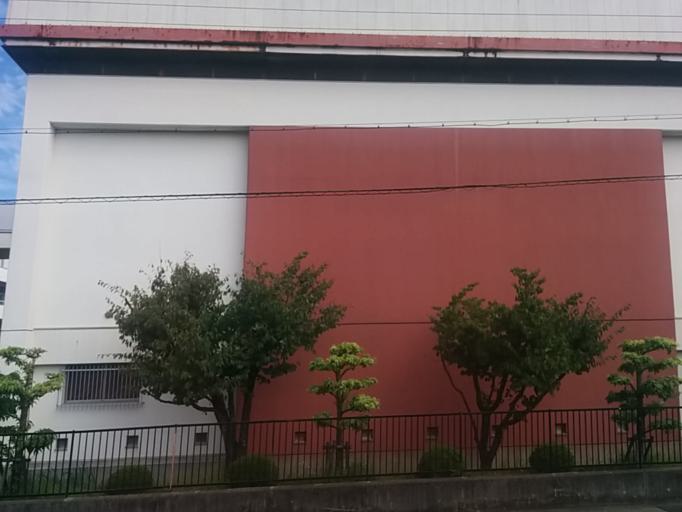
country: JP
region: Nara
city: Kashihara-shi
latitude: 34.4963
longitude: 135.7944
